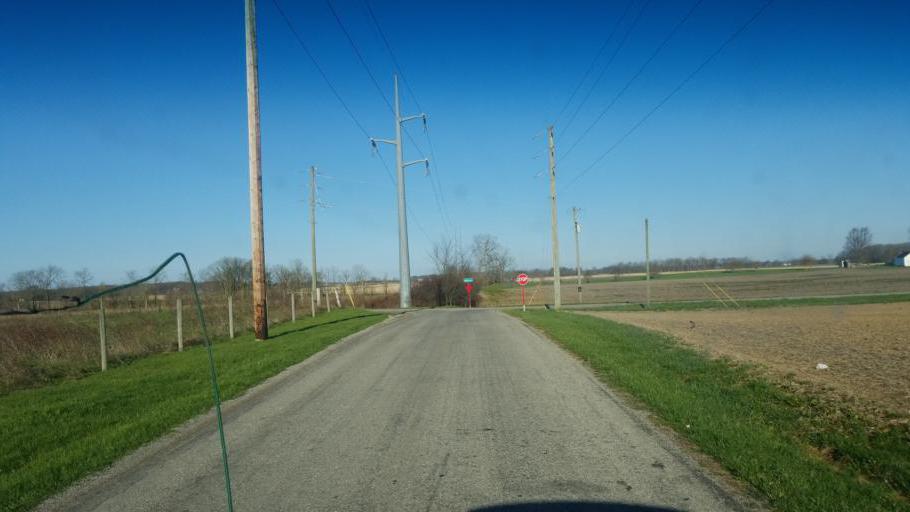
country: US
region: Ohio
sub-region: Union County
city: Richwood
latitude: 40.4465
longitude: -83.4147
